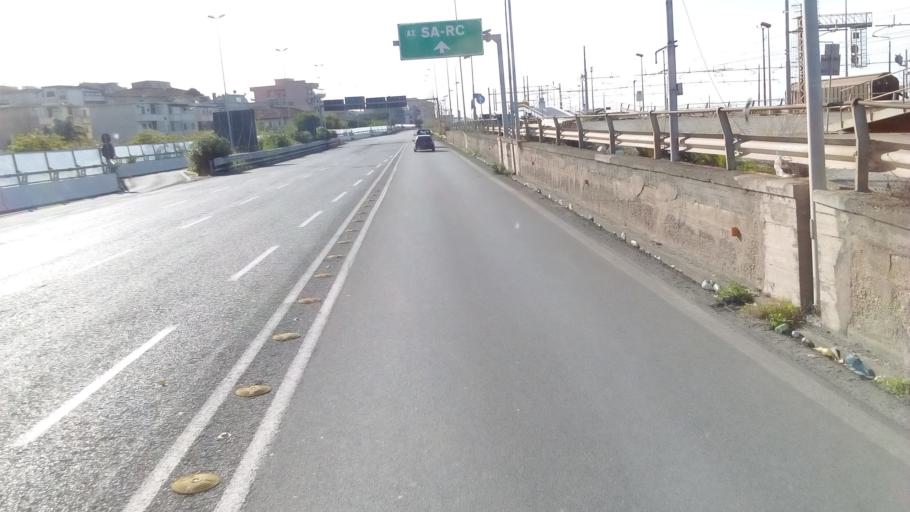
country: IT
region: Calabria
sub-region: Provincia di Reggio Calabria
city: Campo Calabro
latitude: 38.2130
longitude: 15.6352
